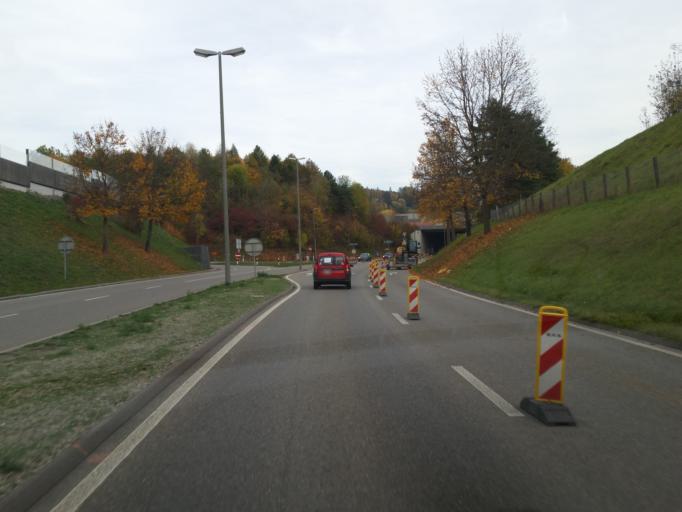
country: CH
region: Zurich
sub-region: Bezirk Winterthur
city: Wuelflingen (Kreis 6) / Haerti
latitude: 47.5154
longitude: 8.6887
